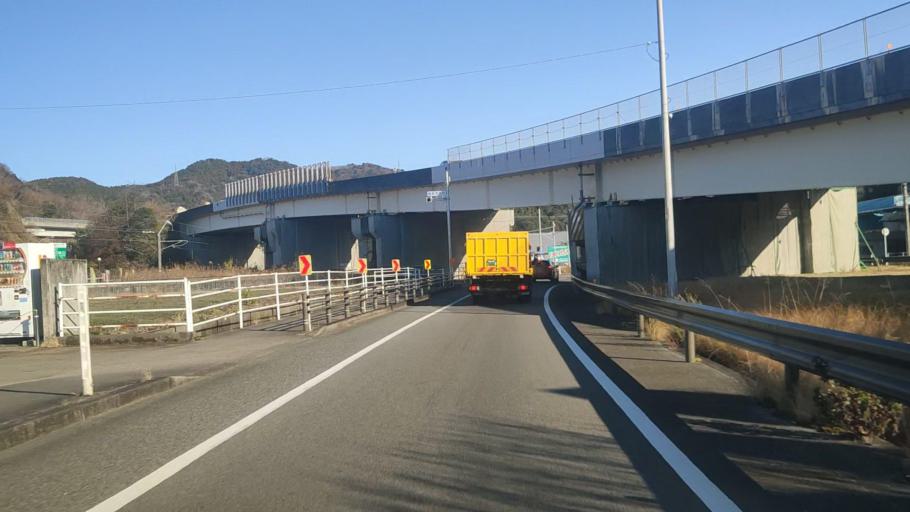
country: JP
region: Miyazaki
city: Nobeoka
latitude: 32.4973
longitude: 131.6623
